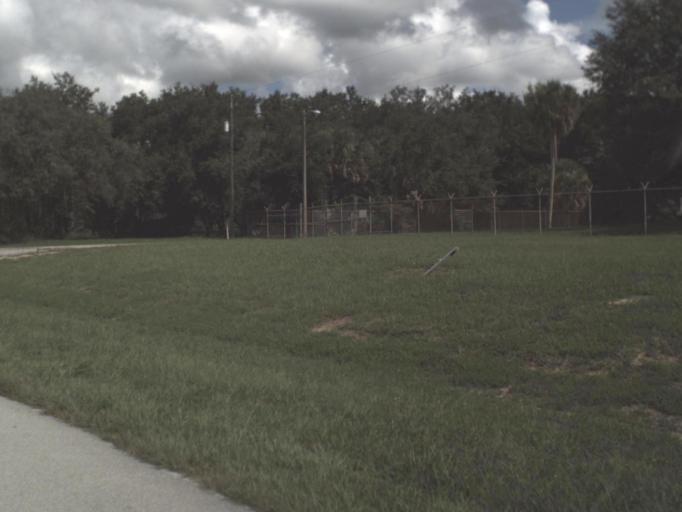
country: US
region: Florida
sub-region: Polk County
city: Polk City
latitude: 28.2941
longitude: -81.8340
